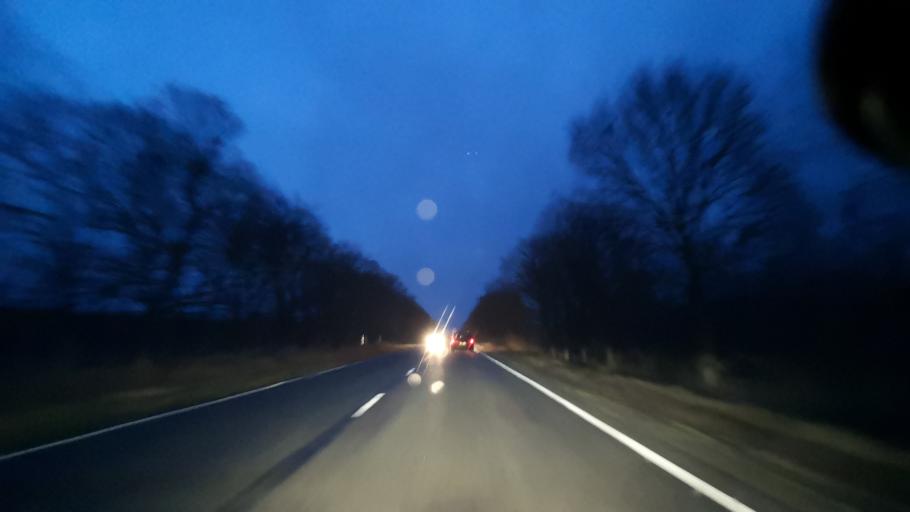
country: MD
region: Orhei
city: Orhei
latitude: 47.4675
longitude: 28.7913
